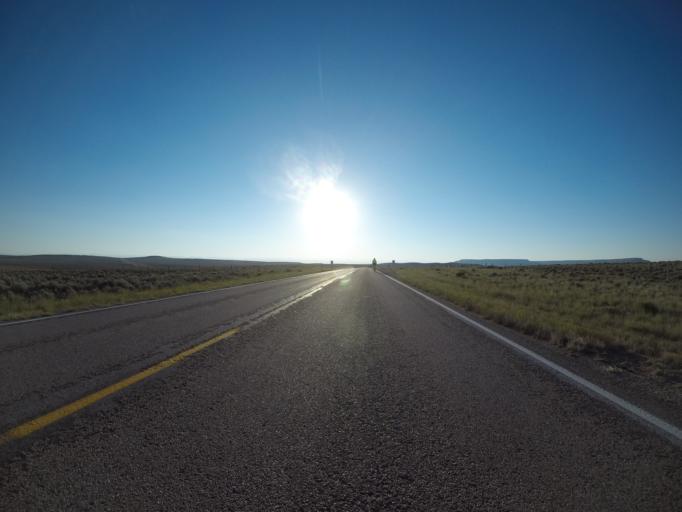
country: US
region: Wyoming
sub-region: Sublette County
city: Marbleton
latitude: 42.5796
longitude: -110.0011
